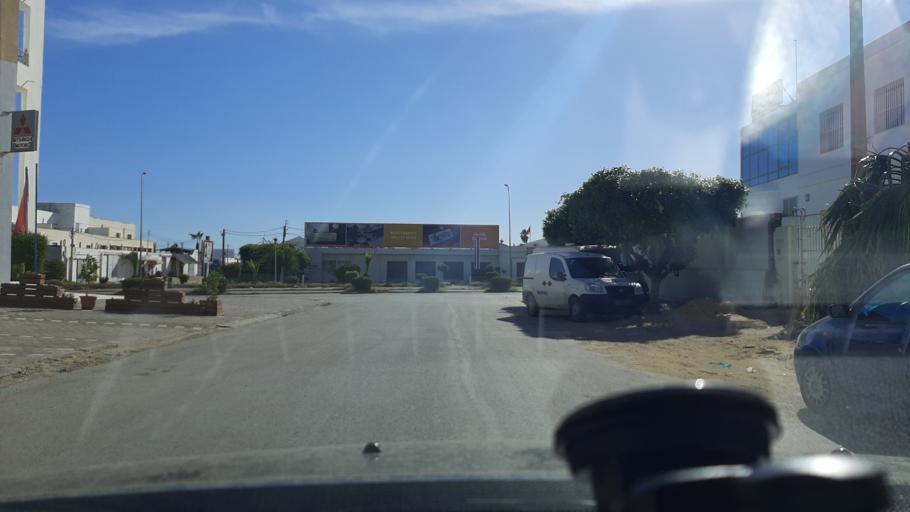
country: TN
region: Safaqis
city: Sfax
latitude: 34.7277
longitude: 10.7419
